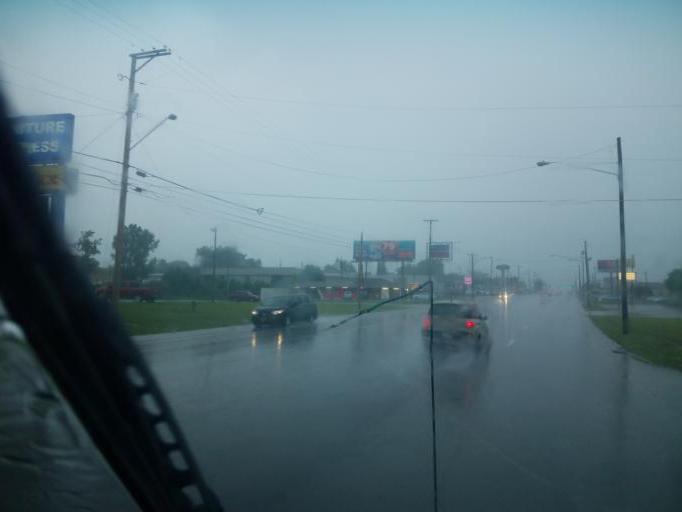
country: US
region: Ohio
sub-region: Stark County
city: Genoa
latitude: 40.7925
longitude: -81.4515
